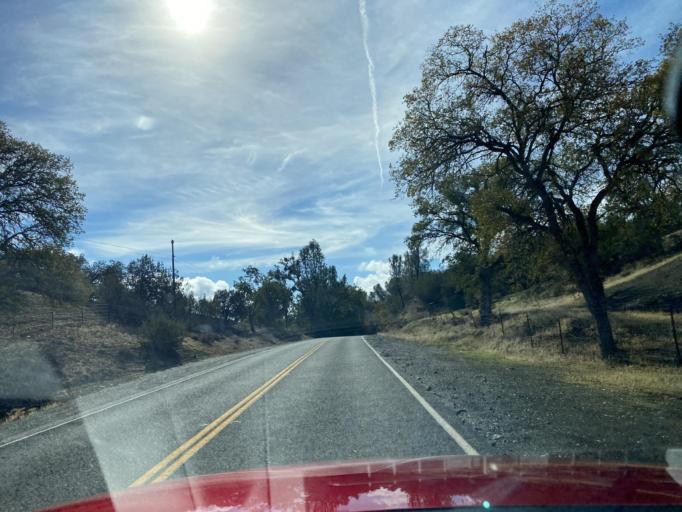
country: US
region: California
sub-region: Glenn County
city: Willows
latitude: 39.4483
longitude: -122.5135
